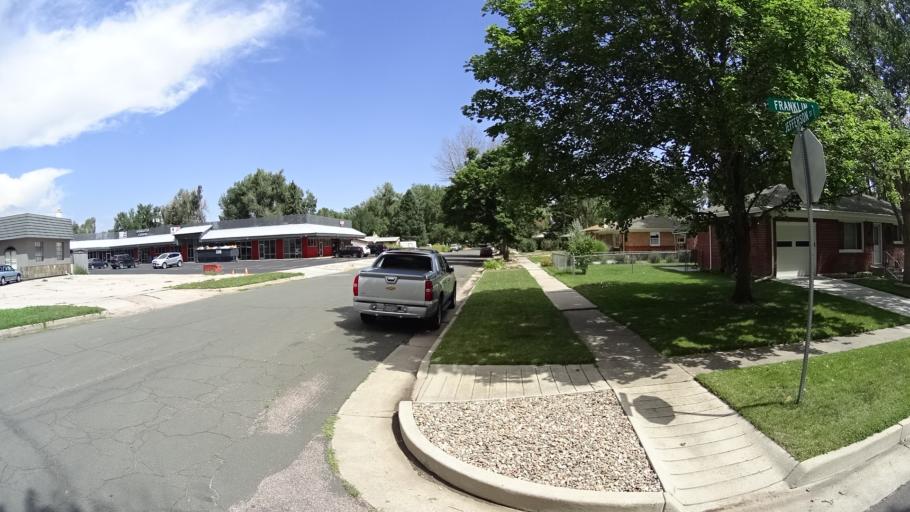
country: US
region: Colorado
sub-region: El Paso County
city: Colorado Springs
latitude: 38.8627
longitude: -104.8105
